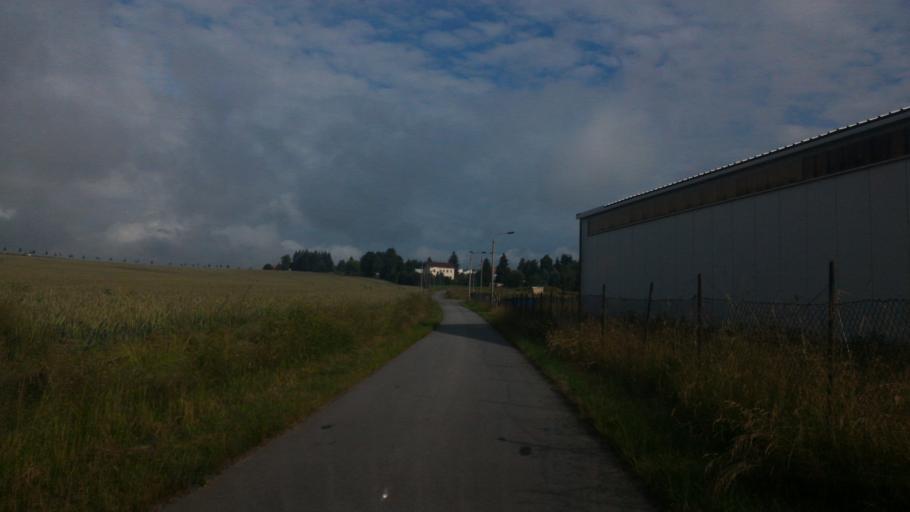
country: DE
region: Saxony
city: Hainewalde
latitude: 50.9433
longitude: 14.6823
